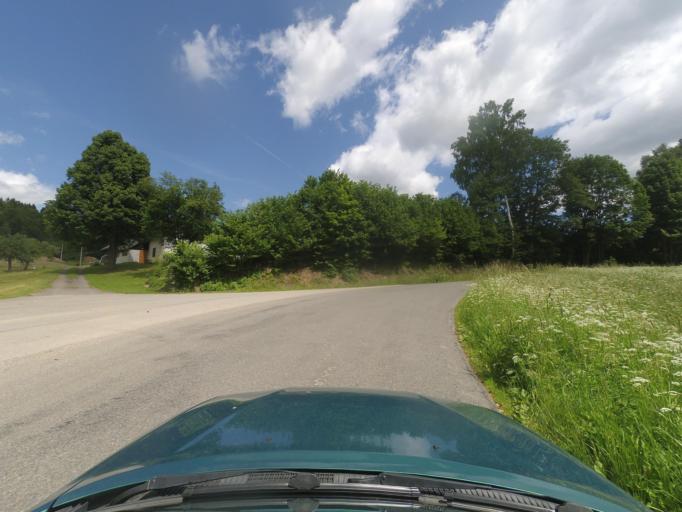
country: CZ
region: Pardubicky
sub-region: Okres Usti nad Orlici
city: Kunvald
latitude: 50.1180
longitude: 16.5722
